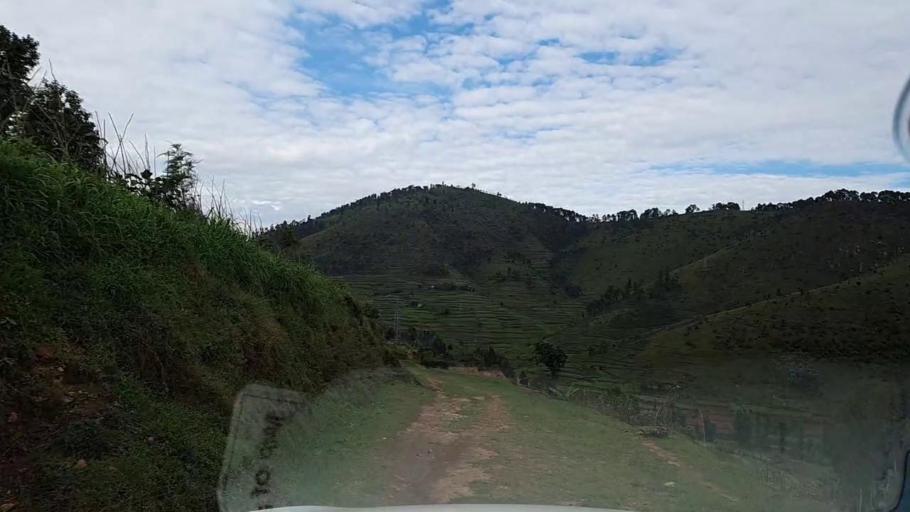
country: RW
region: Southern Province
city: Nzega
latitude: -2.4081
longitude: 29.4950
